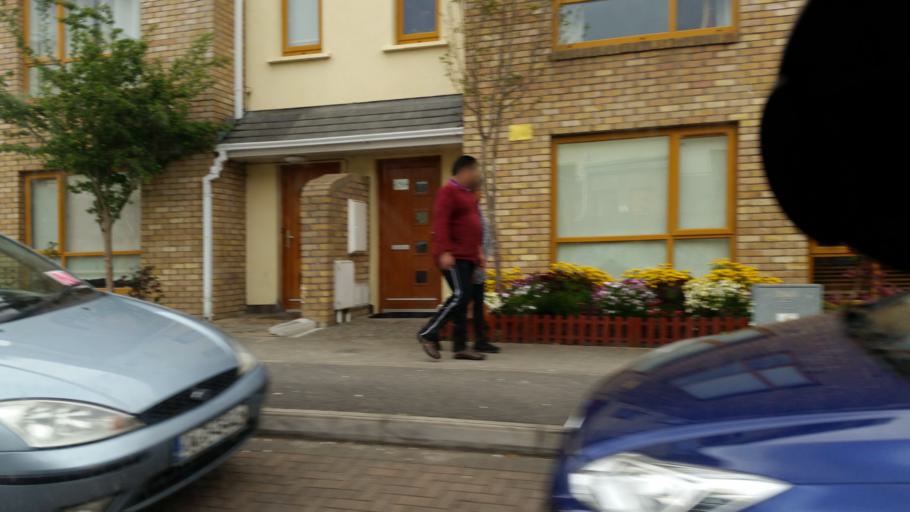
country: IE
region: Leinster
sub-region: Dublin City
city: Finglas
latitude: 53.4047
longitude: -6.2856
